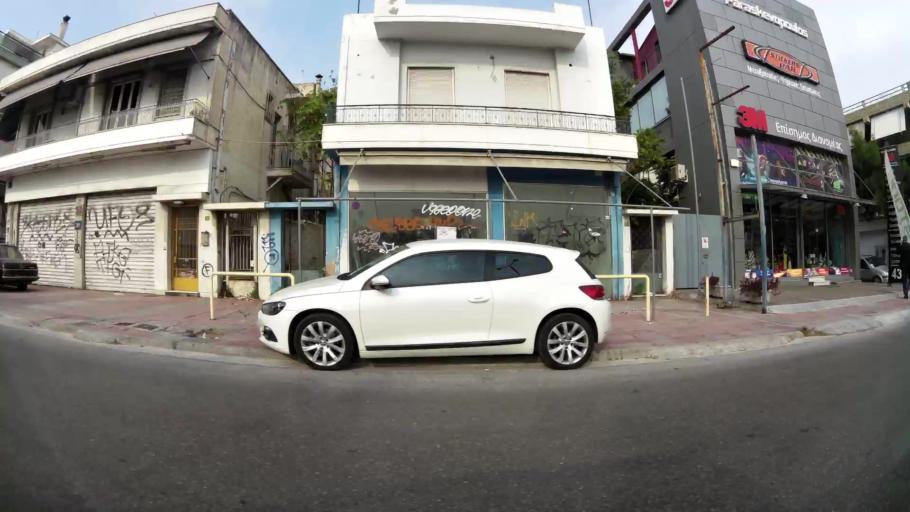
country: GR
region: Attica
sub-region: Nomarchia Athinas
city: Peristeri
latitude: 38.0033
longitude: 23.6866
